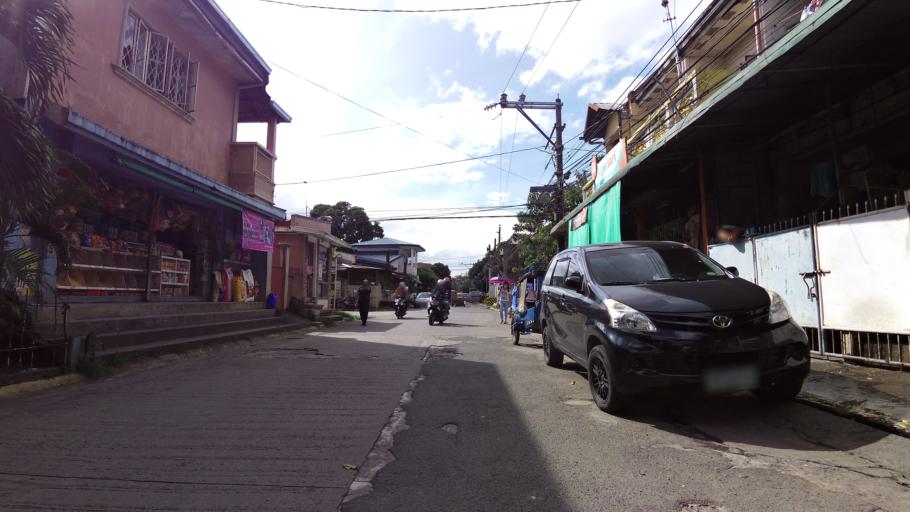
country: PH
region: Calabarzon
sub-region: Province of Rizal
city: Cainta
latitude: 14.5780
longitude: 121.1076
